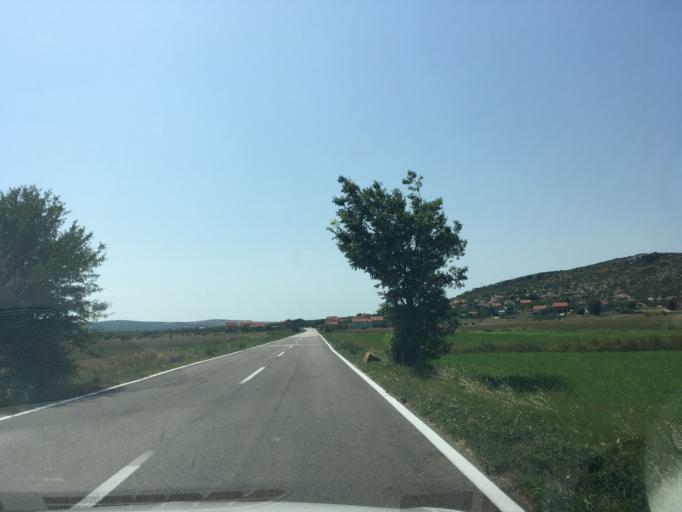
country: HR
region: Zadarska
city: Benkovac
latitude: 43.9632
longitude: 15.7588
